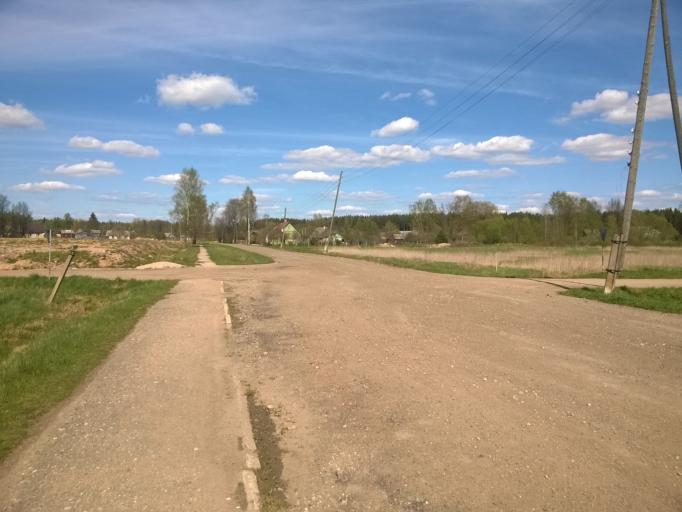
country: LV
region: Vilanu
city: Vilani
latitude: 56.5529
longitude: 26.9310
